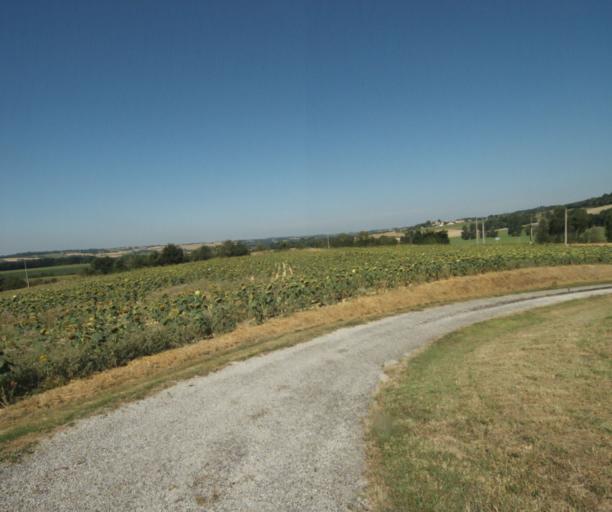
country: FR
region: Midi-Pyrenees
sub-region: Departement de la Haute-Garonne
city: Saint-Felix-Lauragais
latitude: 43.5085
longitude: 1.9261
